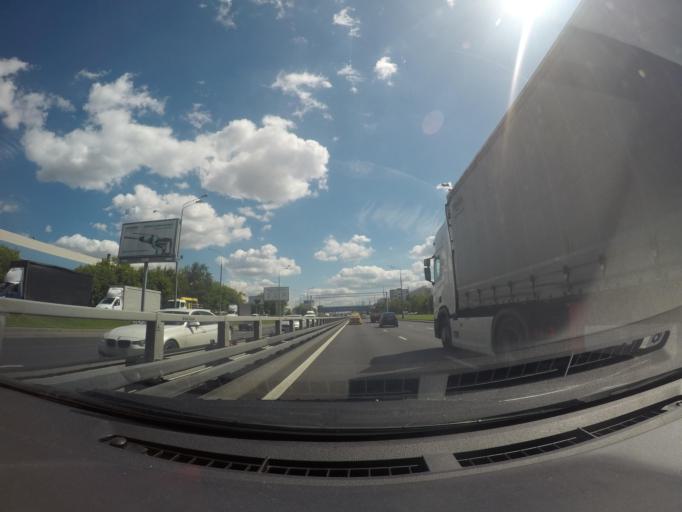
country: RU
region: Moscow
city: Veshnyaki
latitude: 55.7109
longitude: 37.8218
